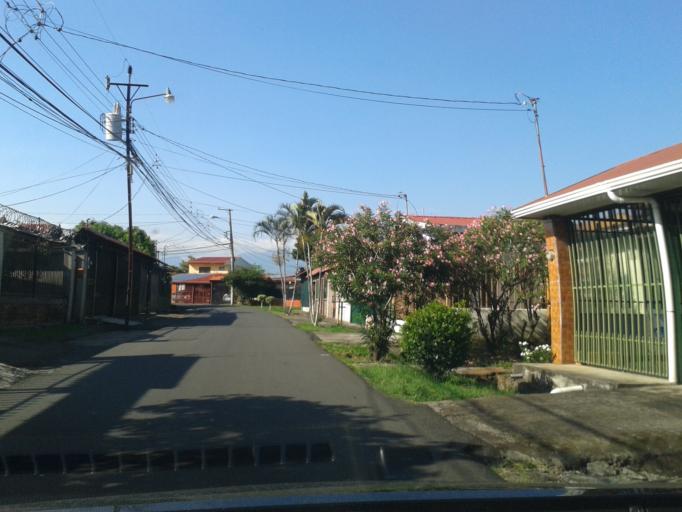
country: CR
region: Heredia
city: Llorente
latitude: 10.0061
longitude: -84.1477
